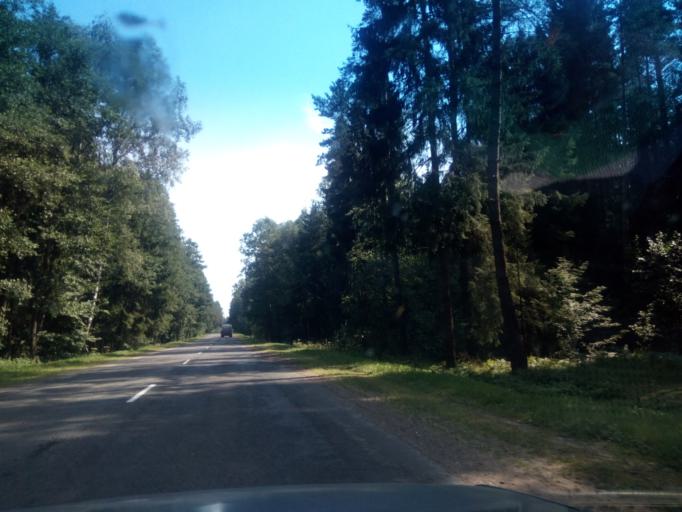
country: BY
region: Vitebsk
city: Vyerkhnyadzvinsk
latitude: 55.7967
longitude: 27.9583
